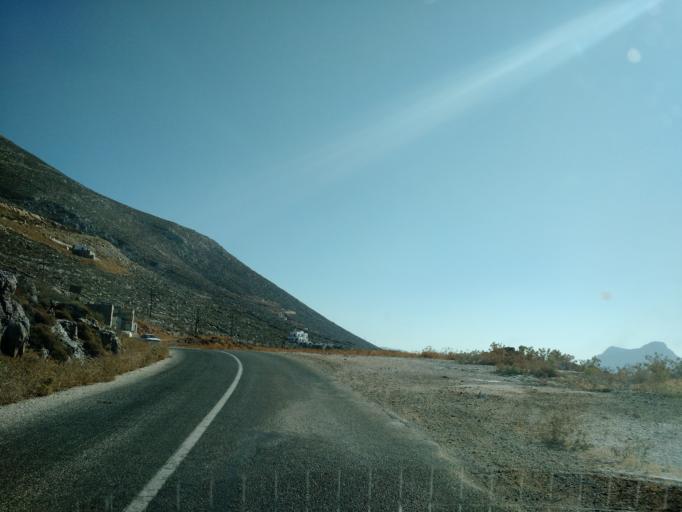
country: GR
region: South Aegean
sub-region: Nomos Kykladon
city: Amorgos
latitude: 36.8968
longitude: 25.9697
